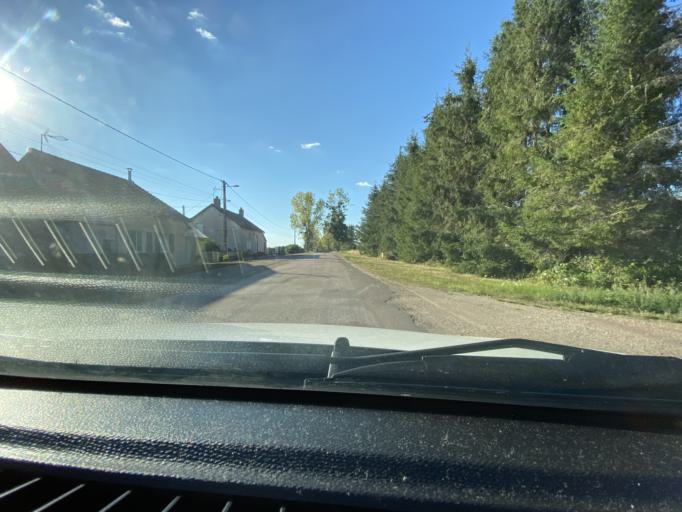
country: FR
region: Bourgogne
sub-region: Departement de la Cote-d'Or
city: Saulieu
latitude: 47.3175
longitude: 4.1994
